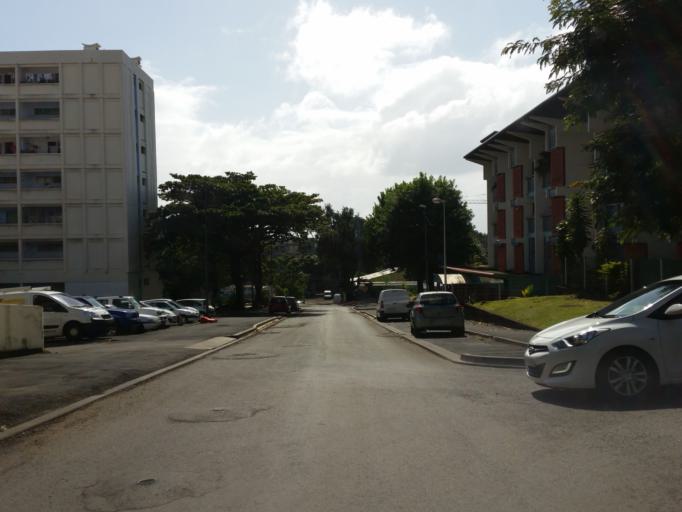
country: RE
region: Reunion
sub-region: Reunion
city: Saint-Denis
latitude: -20.8934
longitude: 55.4625
